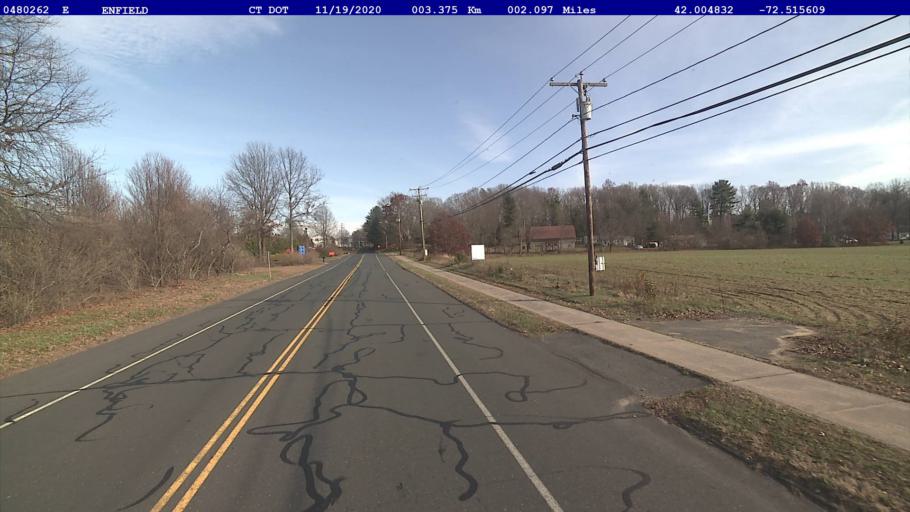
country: US
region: Connecticut
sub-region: Hartford County
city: Hazardville
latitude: 42.0048
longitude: -72.5156
